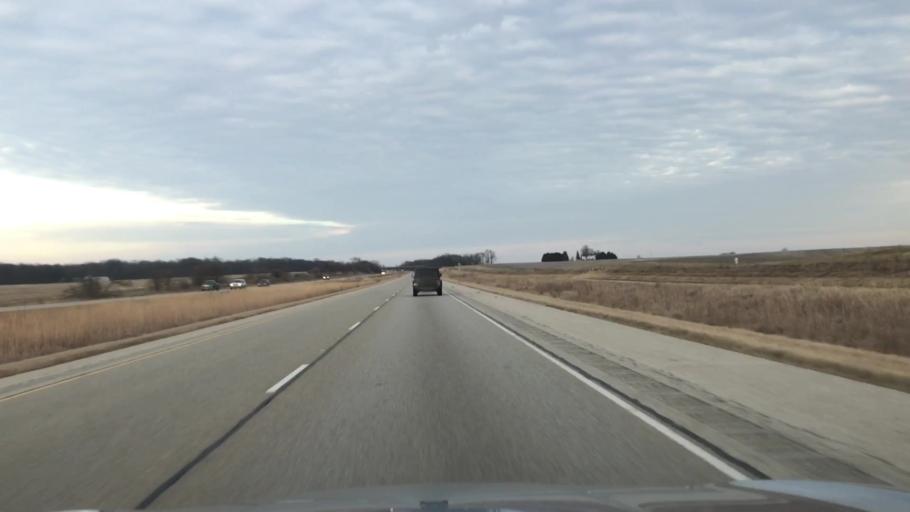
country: US
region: Illinois
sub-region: Logan County
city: Atlanta
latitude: 40.3477
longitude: -89.1260
